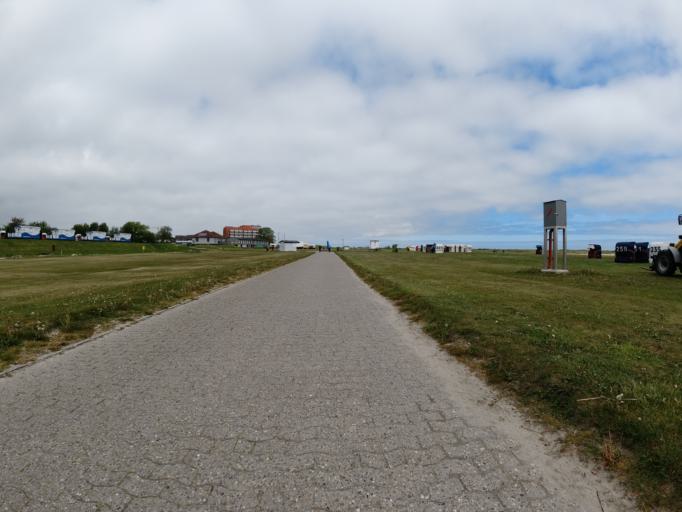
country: DE
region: Lower Saxony
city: Schillig
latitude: 53.7014
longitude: 8.0288
